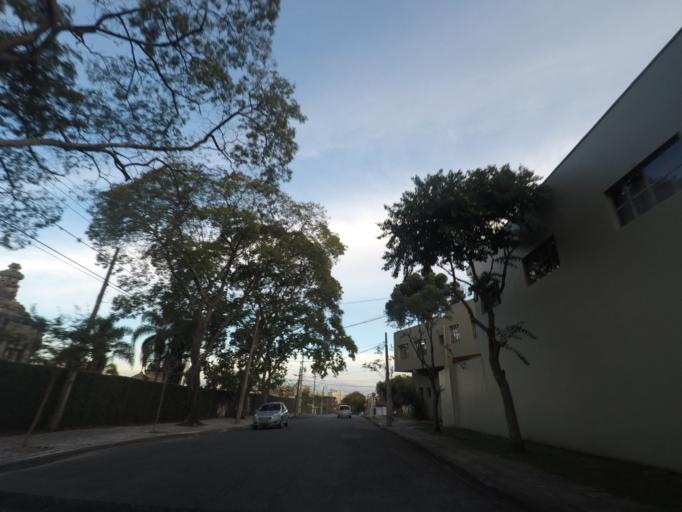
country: BR
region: Parana
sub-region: Curitiba
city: Curitiba
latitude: -25.4196
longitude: -49.2775
